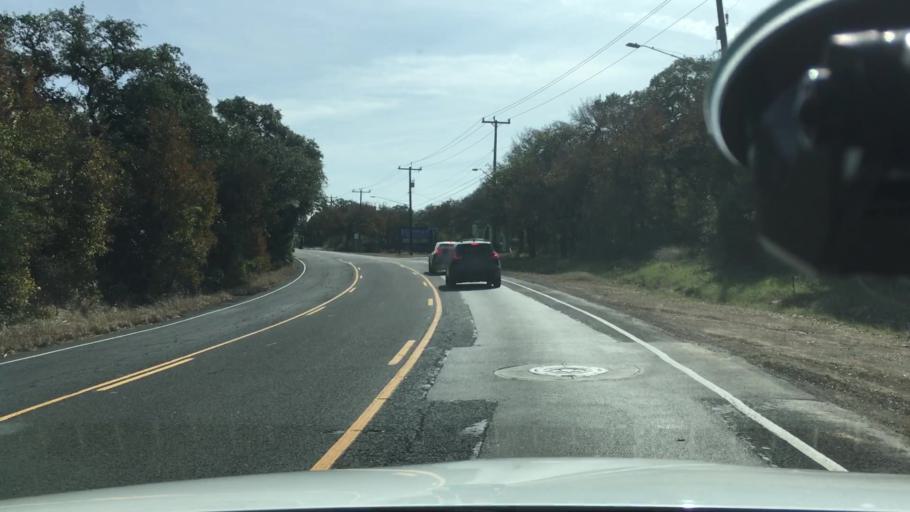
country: US
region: Texas
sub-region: Bexar County
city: Hollywood Park
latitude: 29.5845
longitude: -98.4233
